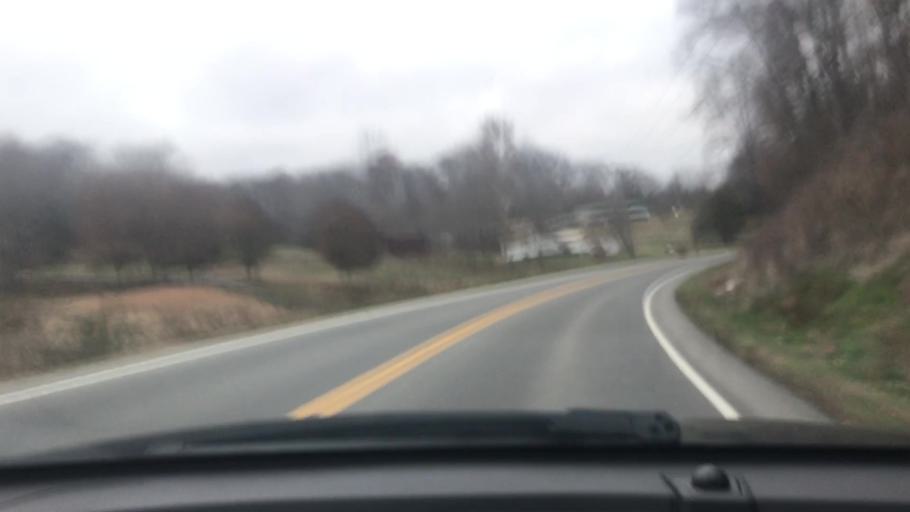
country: US
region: Tennessee
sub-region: Dickson County
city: Charlotte
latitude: 36.2437
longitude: -87.3478
